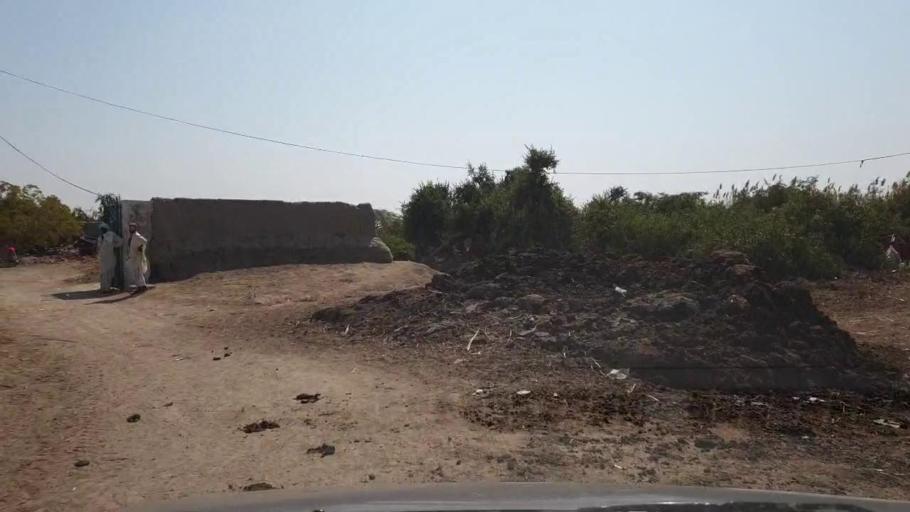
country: PK
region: Sindh
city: Samaro
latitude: 25.2312
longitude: 69.2536
